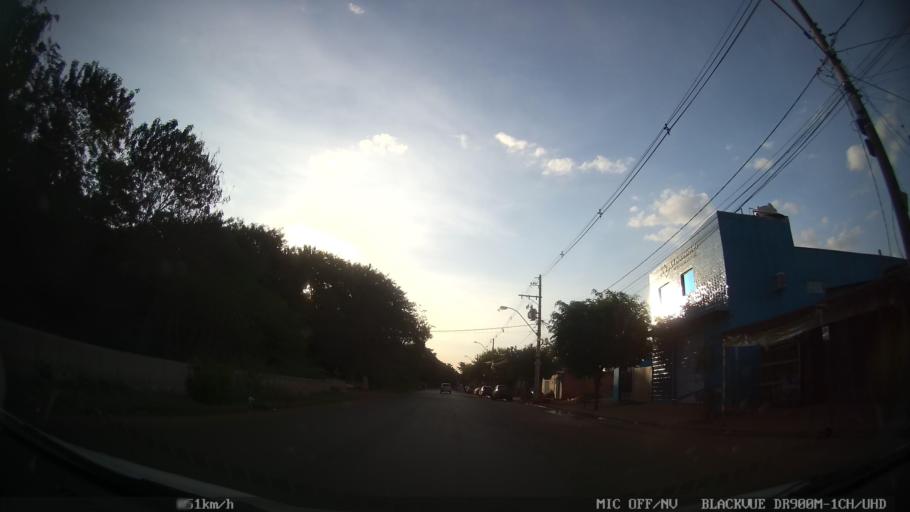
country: BR
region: Sao Paulo
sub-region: Ribeirao Preto
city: Ribeirao Preto
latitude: -21.1143
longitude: -47.8051
